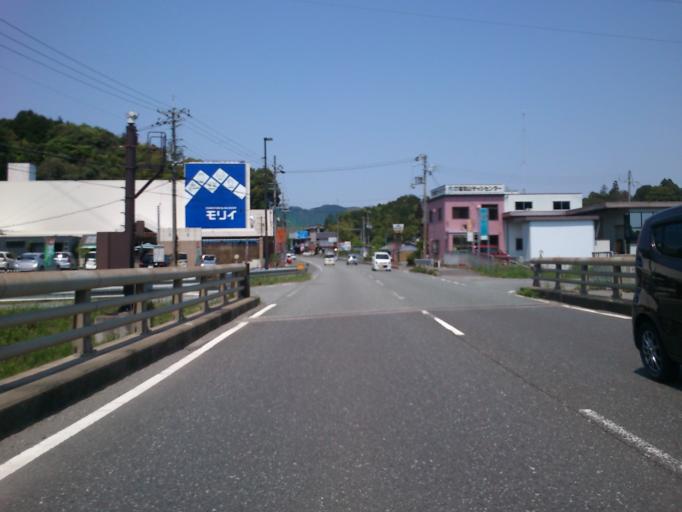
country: JP
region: Kyoto
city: Fukuchiyama
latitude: 35.3096
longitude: 135.1032
